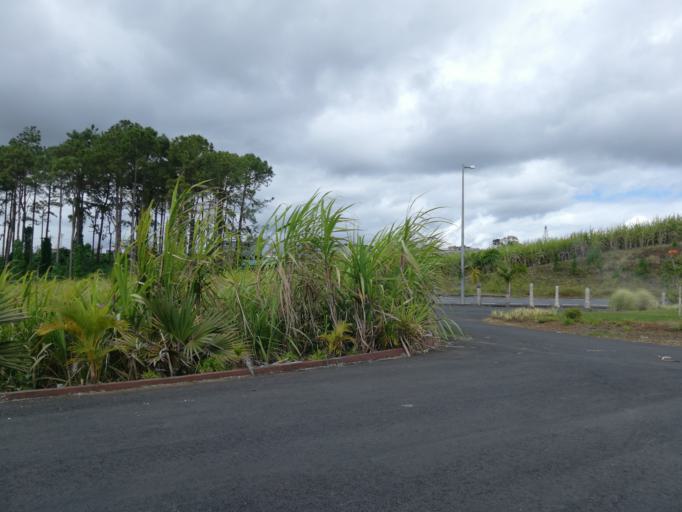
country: MU
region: Moka
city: Quartier Militaire
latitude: -20.2431
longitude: 57.5939
